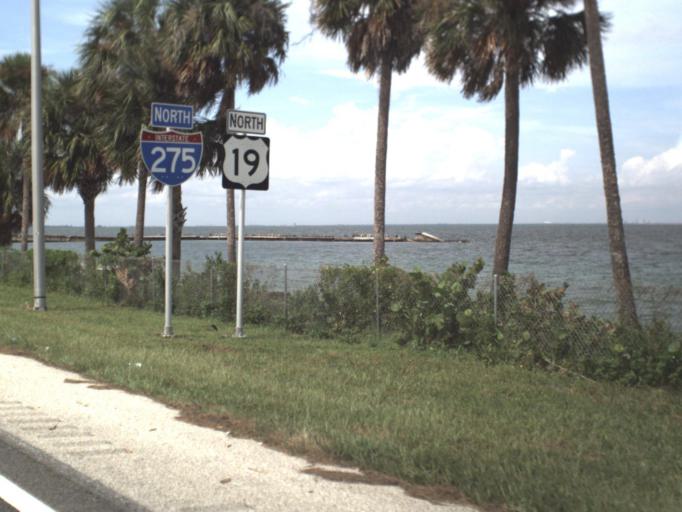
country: US
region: Florida
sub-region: Manatee County
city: Memphis
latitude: 27.5883
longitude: -82.6229
